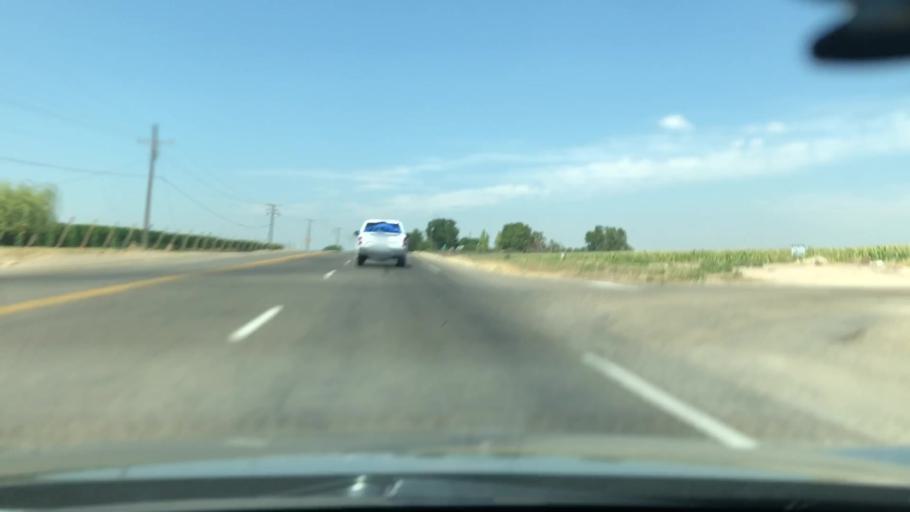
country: US
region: Idaho
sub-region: Canyon County
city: Wilder
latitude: 43.6613
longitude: -116.9117
